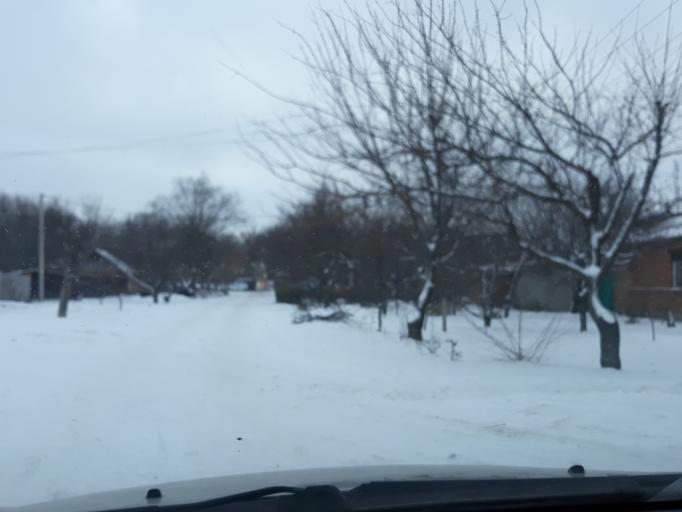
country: RU
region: Rostov
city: Taganrog
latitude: 47.2291
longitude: 38.8903
